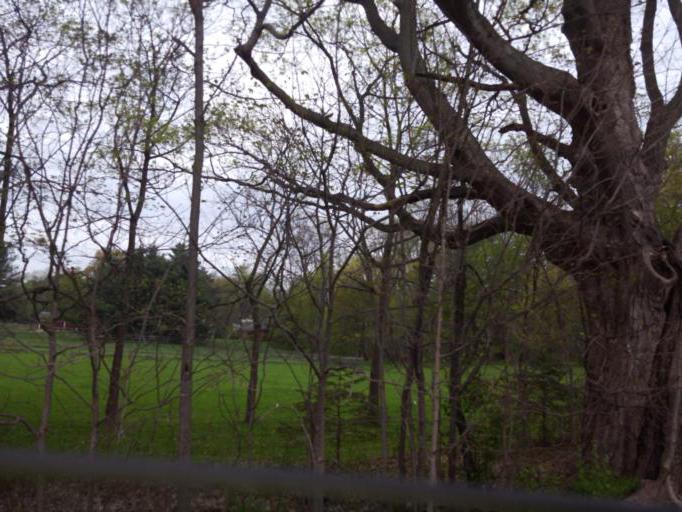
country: US
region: Ohio
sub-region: Richland County
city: Lexington
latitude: 40.7129
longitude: -82.6064
